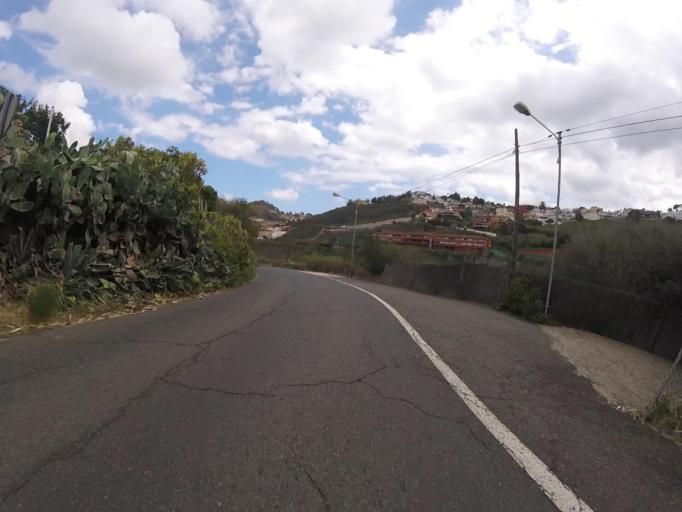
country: ES
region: Canary Islands
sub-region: Provincia de Las Palmas
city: Santa Brigida
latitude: 28.0476
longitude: -15.4824
